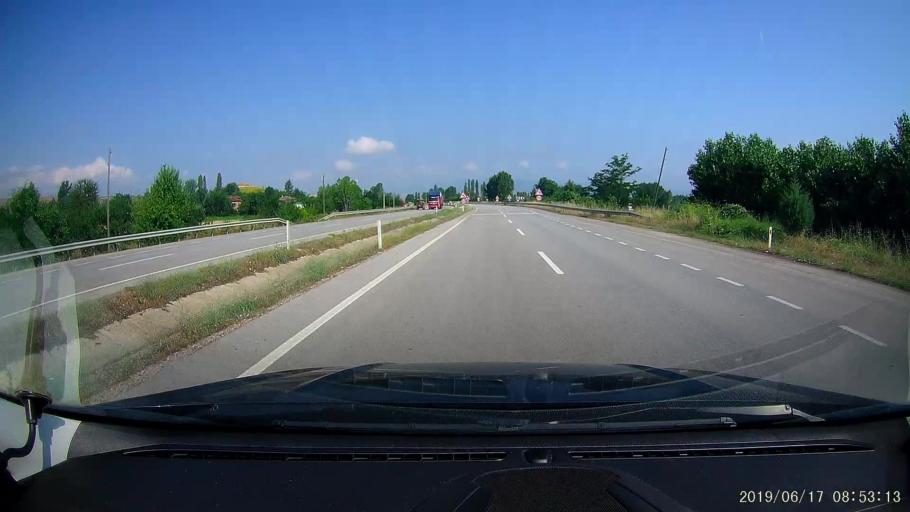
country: TR
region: Tokat
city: Erbaa
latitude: 40.7075
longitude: 36.4849
